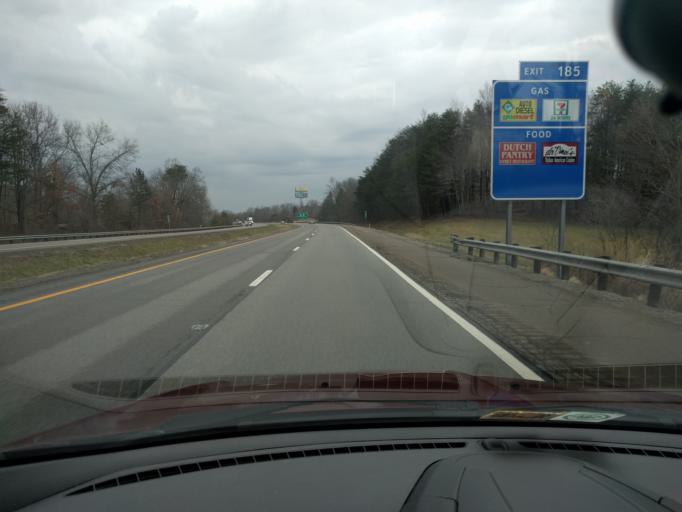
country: US
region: West Virginia
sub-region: Wood County
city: Williamstown
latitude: 39.3680
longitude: -81.4395
